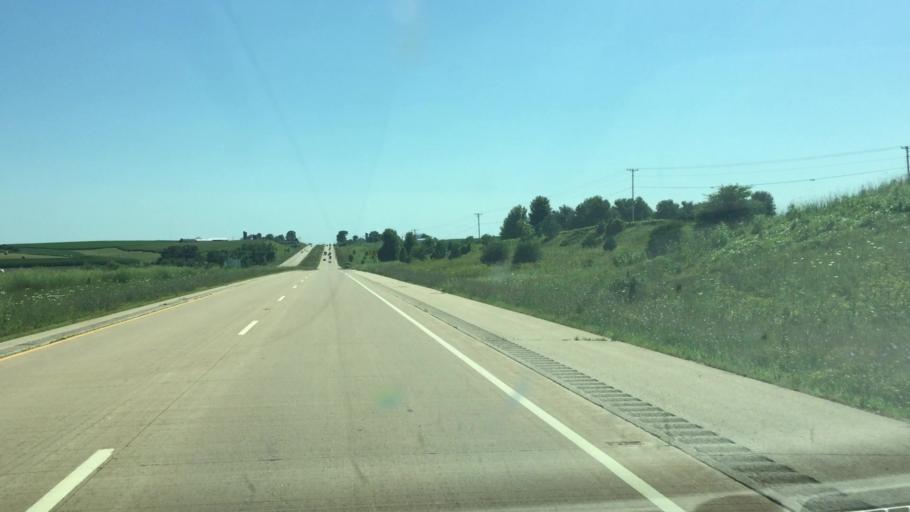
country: US
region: Wisconsin
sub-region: Grant County
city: Dickeyville
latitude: 42.6159
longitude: -90.5870
